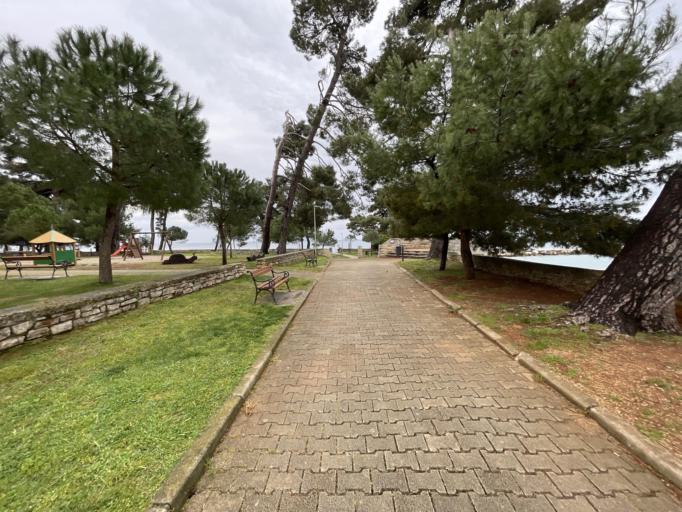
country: HR
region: Istarska
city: Novigrad
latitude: 45.3163
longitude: 13.5576
